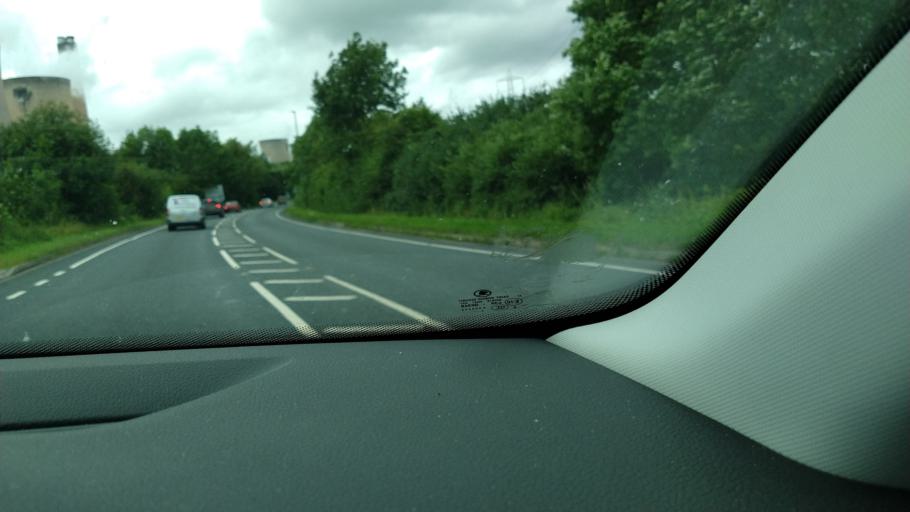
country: GB
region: England
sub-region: North Yorkshire
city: Camblesforth
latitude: 53.7278
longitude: -0.9919
